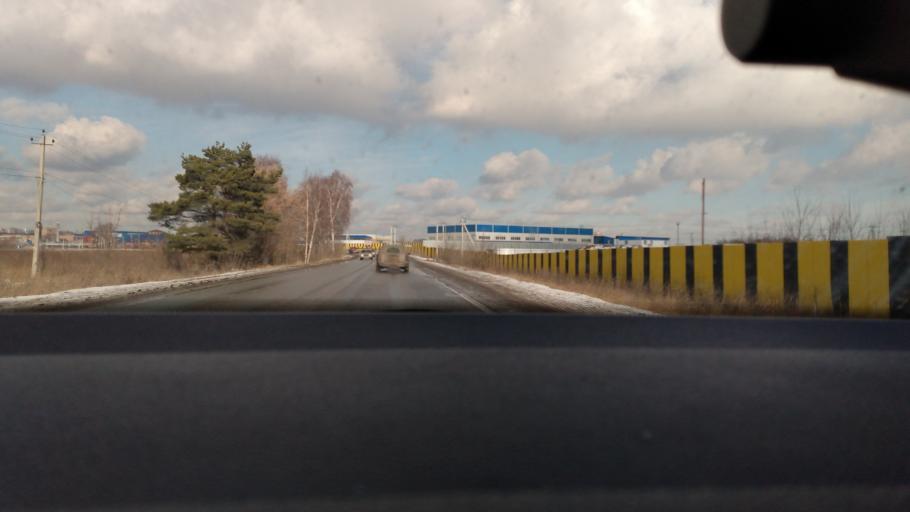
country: RU
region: Moskovskaya
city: Chornaya
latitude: 55.7150
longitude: 38.0461
